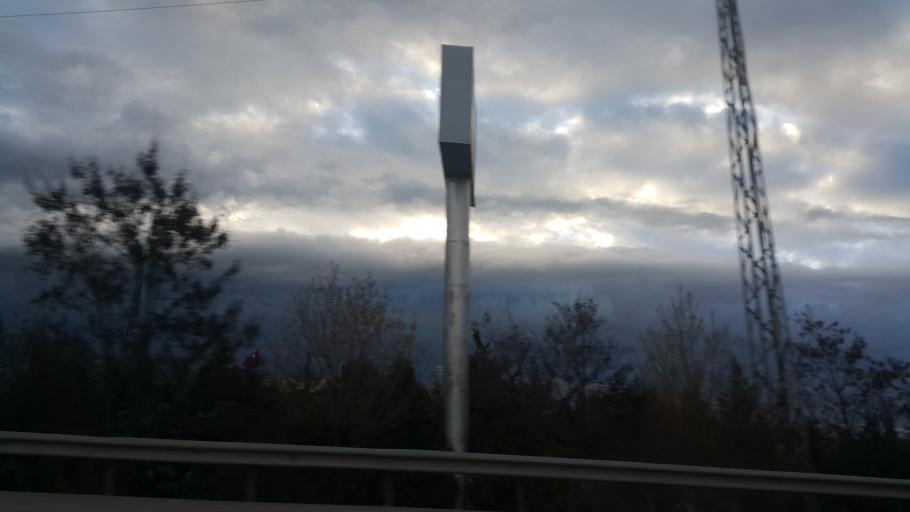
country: TR
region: Ankara
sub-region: Goelbasi
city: Golbasi
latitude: 39.7557
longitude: 32.8043
